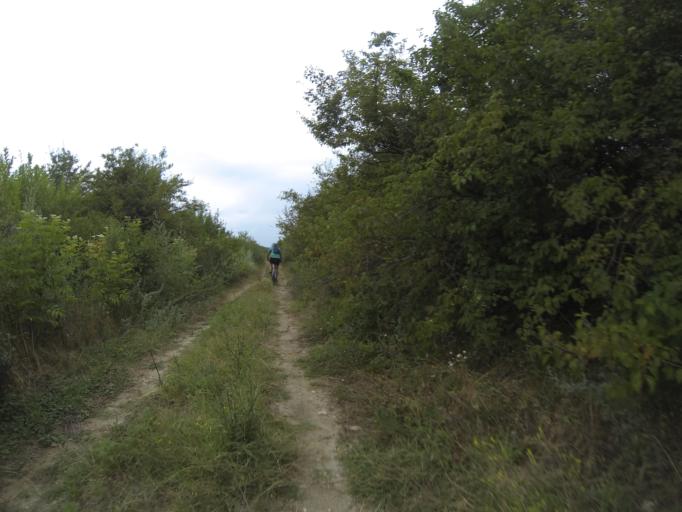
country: RO
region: Dolj
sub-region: Comuna Cotofenii din Fata
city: Cotofenii din Fata
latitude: 44.4817
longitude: 23.6858
